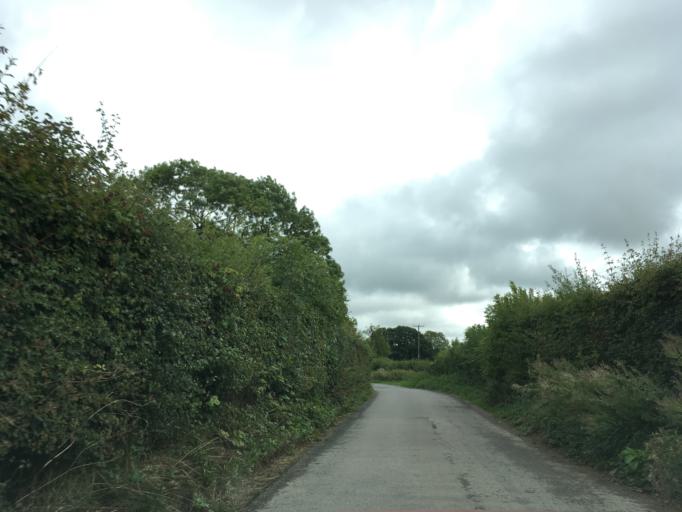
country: GB
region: England
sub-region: South Gloucestershire
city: Chipping Sodbury
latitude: 51.5250
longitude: -2.3882
